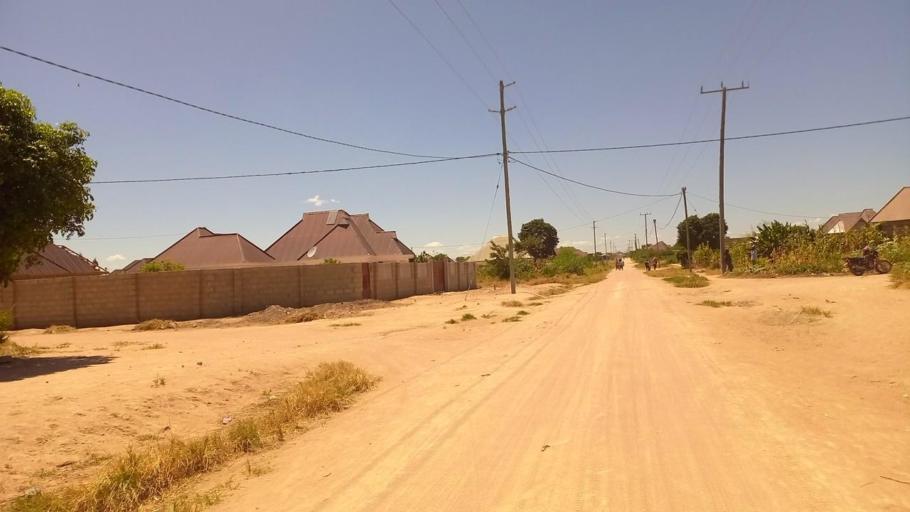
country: TZ
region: Dodoma
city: Dodoma
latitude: -6.1325
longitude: 35.7200
